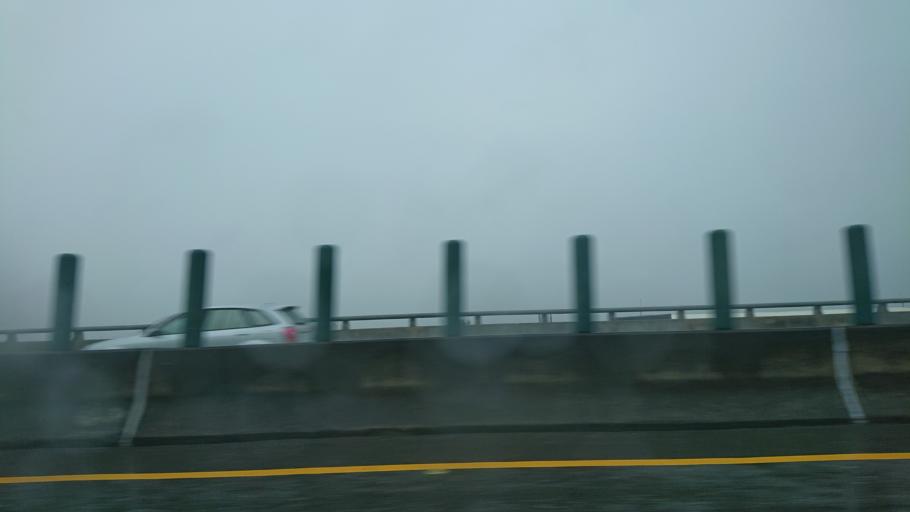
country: TW
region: Taiwan
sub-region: Yunlin
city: Douliu
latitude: 23.7932
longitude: 120.2776
